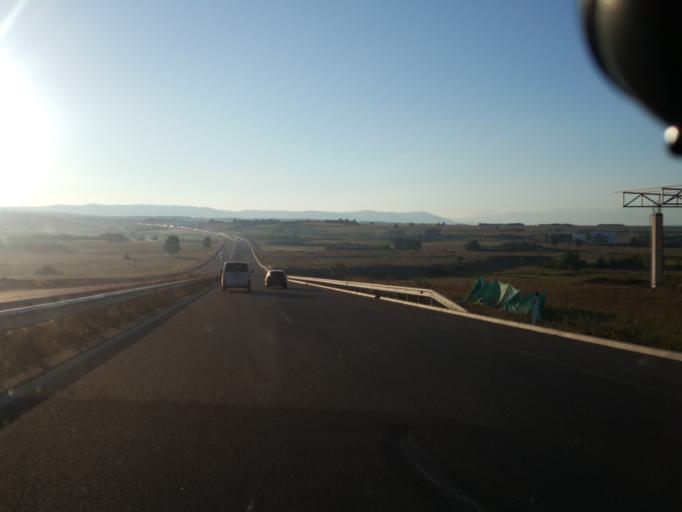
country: XK
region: Prizren
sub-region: Komuna e Malisheves
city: Llazice
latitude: 42.5735
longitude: 20.7270
